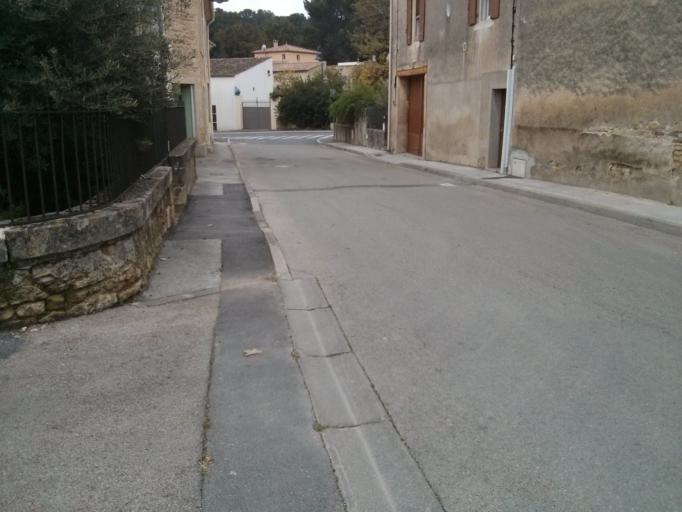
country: FR
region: Languedoc-Roussillon
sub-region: Departement du Gard
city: Aigues-Vives
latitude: 43.7367
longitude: 4.1810
